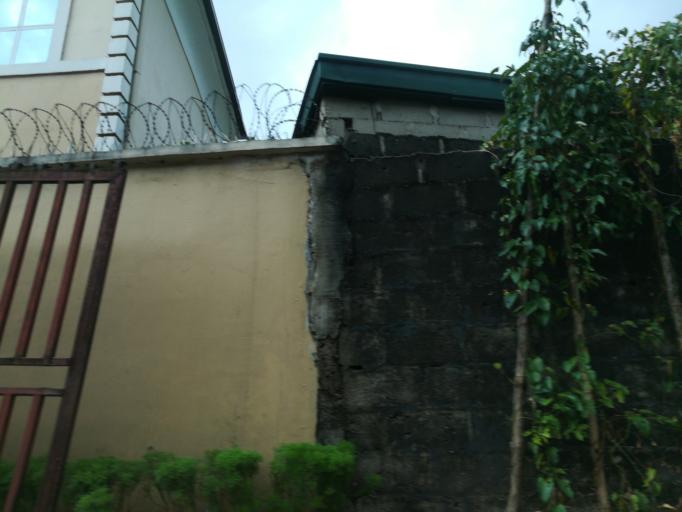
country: NG
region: Rivers
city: Port Harcourt
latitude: 4.8221
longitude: 7.0662
